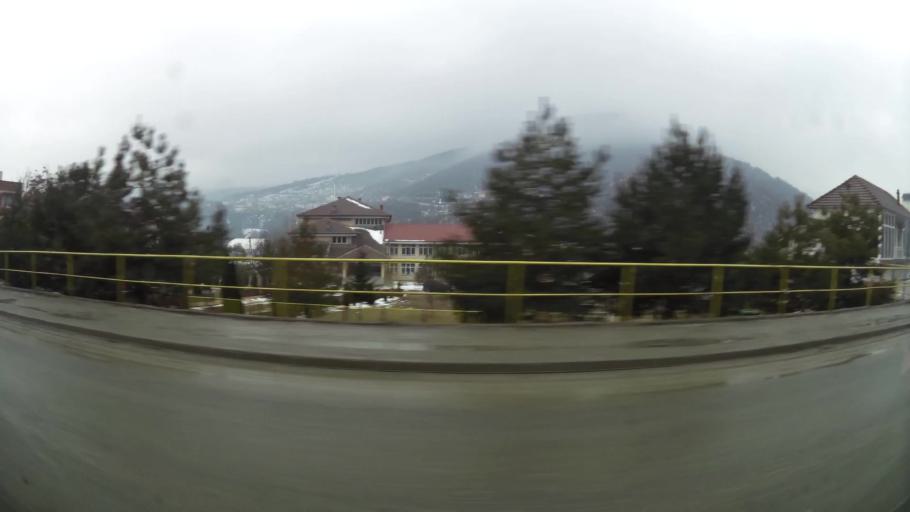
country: XK
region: Ferizaj
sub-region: Hani i Elezit
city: Hani i Elezit
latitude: 42.1540
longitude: 21.2966
